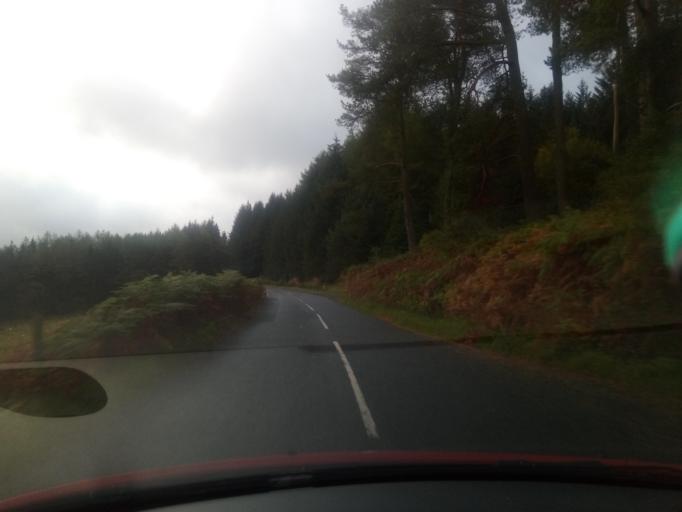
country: GB
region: Scotland
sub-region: The Scottish Borders
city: Hawick
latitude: 55.3377
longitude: -2.6511
